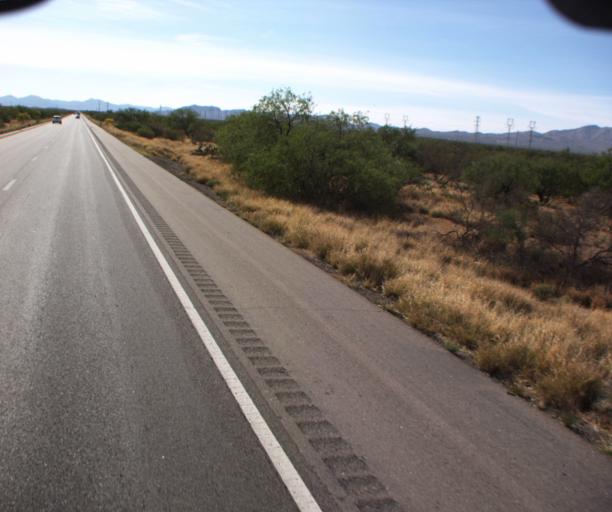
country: US
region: Arizona
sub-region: Pima County
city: Vail
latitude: 32.0435
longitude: -110.7454
